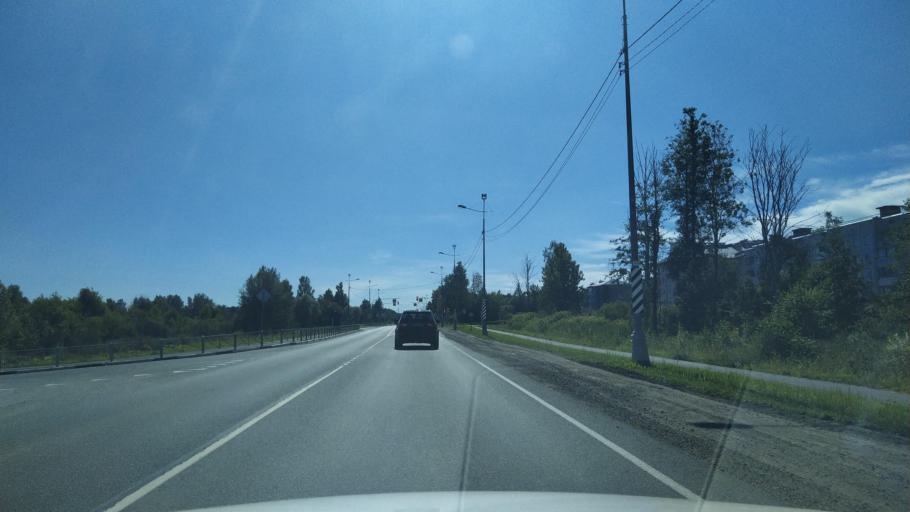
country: RU
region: Pskov
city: Pskov
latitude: 57.7917
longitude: 28.4139
